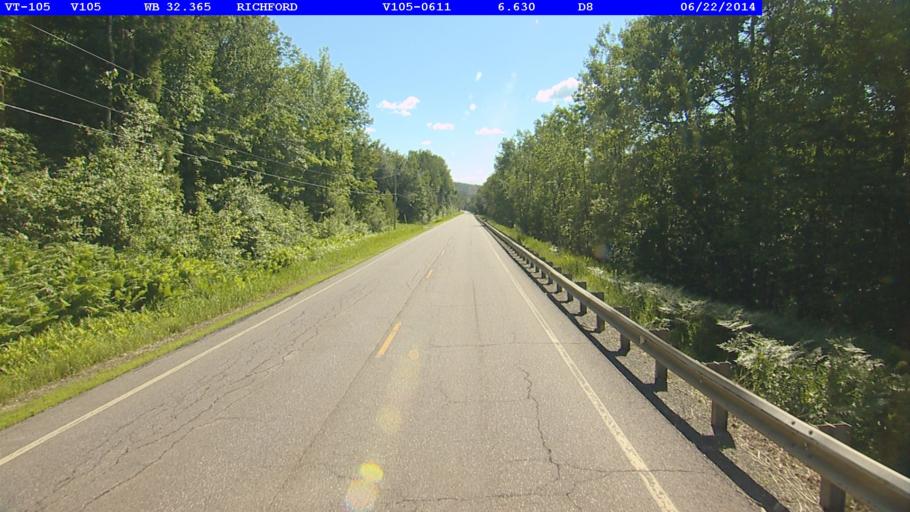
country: US
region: Vermont
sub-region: Franklin County
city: Richford
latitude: 45.0029
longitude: -72.5912
